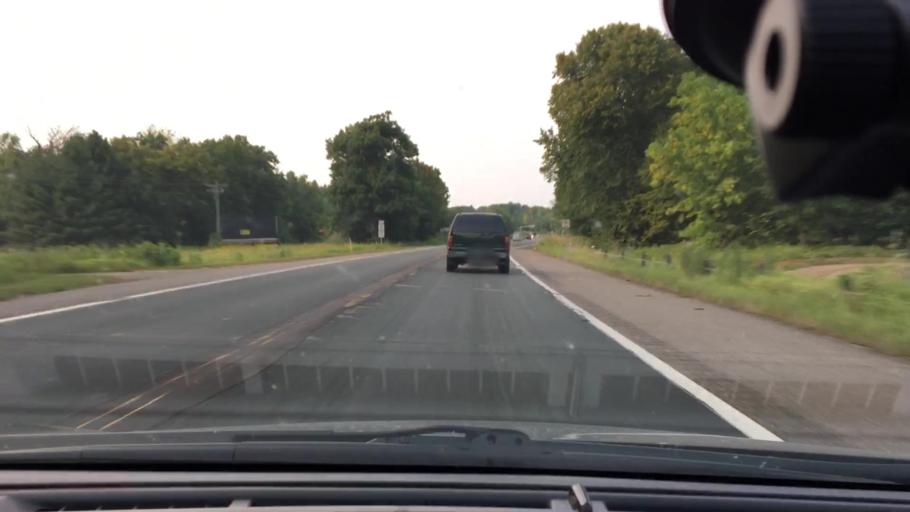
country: US
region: Minnesota
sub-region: Mille Lacs County
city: Vineland
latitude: 46.2169
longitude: -93.7928
